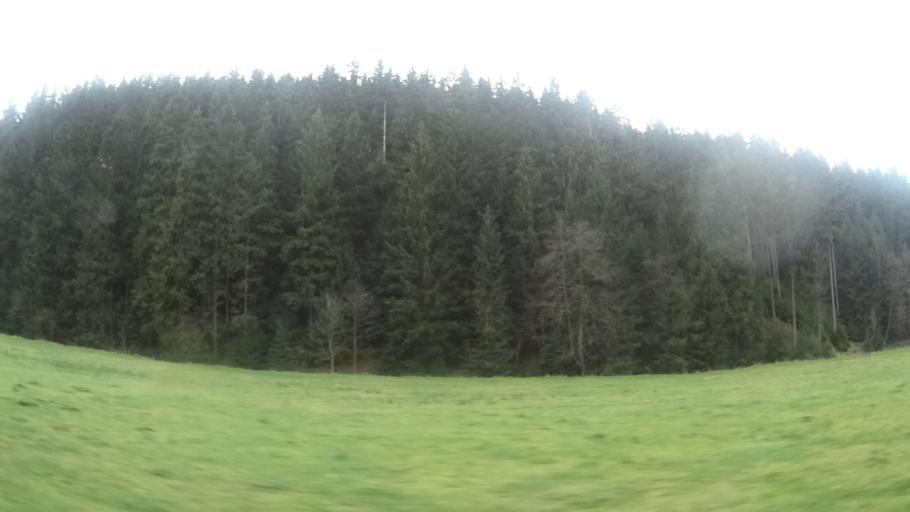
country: DE
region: Thuringia
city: Wittgendorf
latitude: 50.5952
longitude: 11.2386
